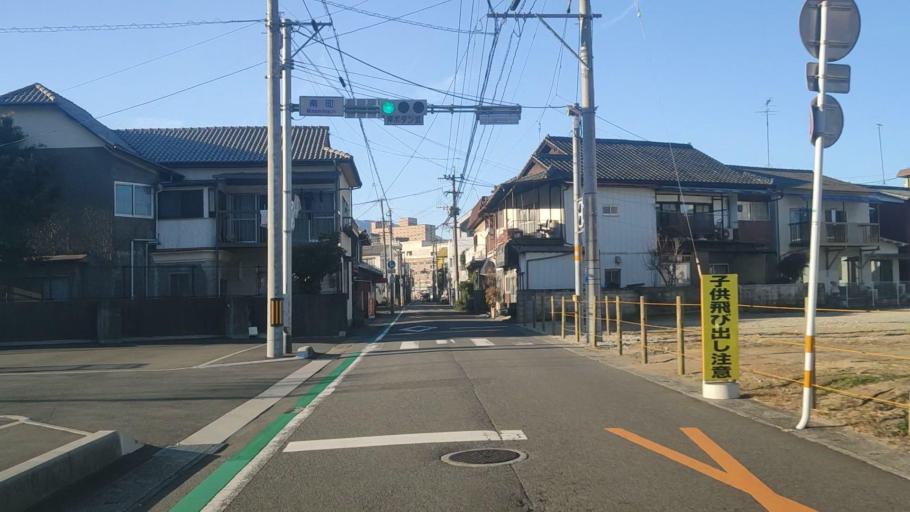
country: JP
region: Oita
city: Beppu
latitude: 33.2713
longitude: 131.5052
